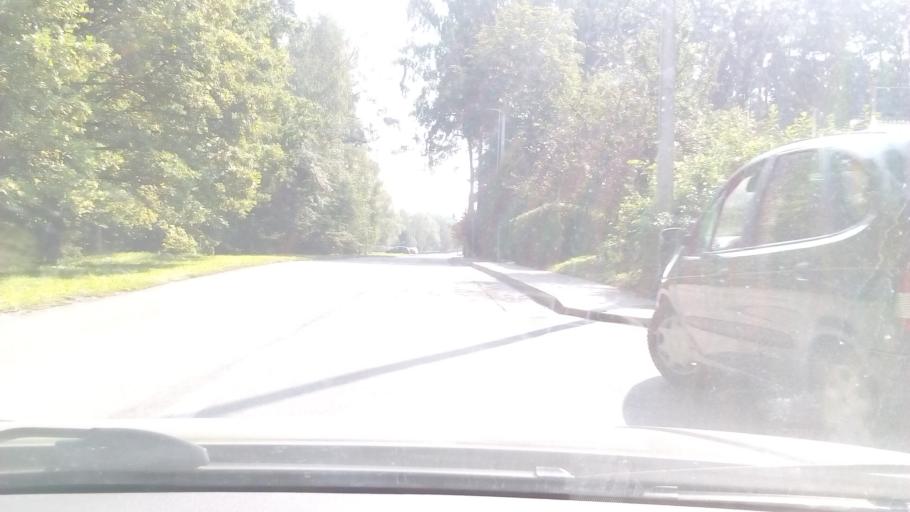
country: LT
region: Alytaus apskritis
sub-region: Alytus
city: Alytus
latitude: 54.3918
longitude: 24.0594
